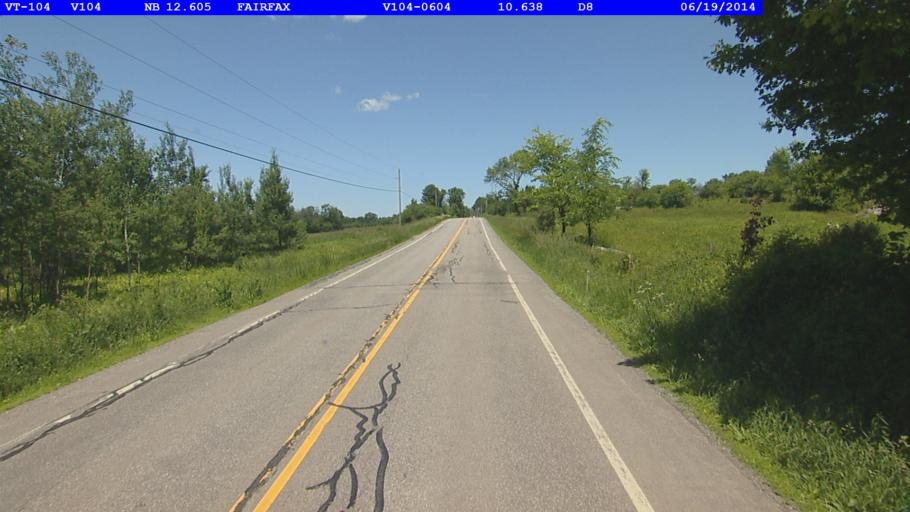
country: US
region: Vermont
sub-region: Franklin County
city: Saint Albans
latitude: 44.7372
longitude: -73.0491
